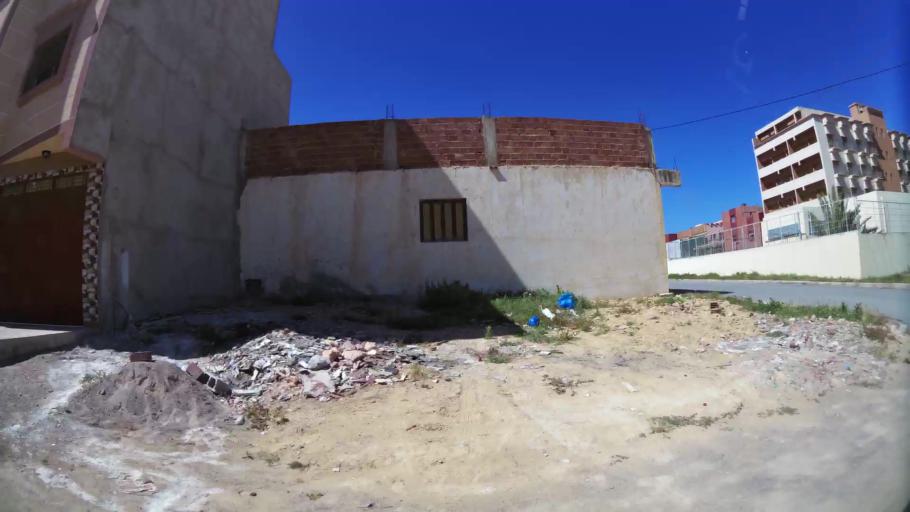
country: MA
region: Oriental
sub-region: Berkane-Taourirt
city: Madagh
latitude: 35.1381
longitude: -2.4249
